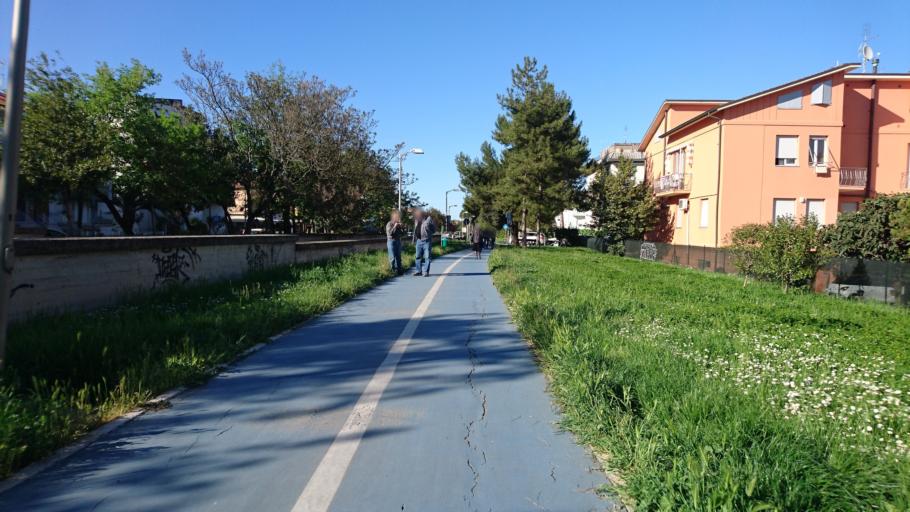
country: IT
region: The Marches
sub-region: Provincia di Pesaro e Urbino
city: Pesaro
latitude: 43.8974
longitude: 12.9114
